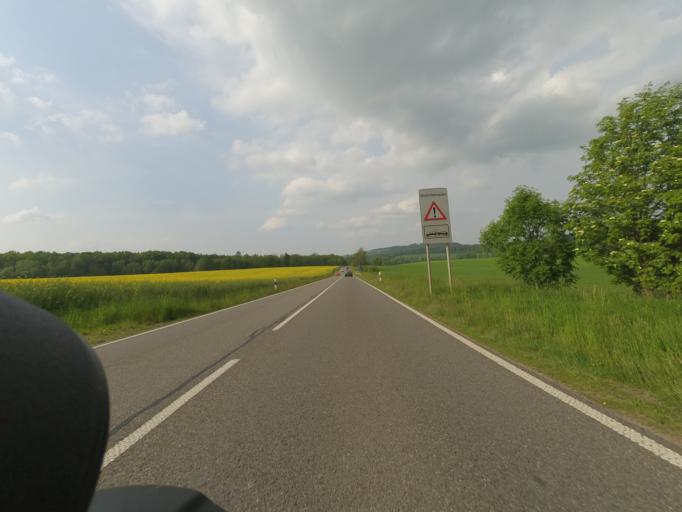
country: DE
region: Saxony
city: Dippoldiswalde
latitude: 50.9123
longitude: 13.6993
